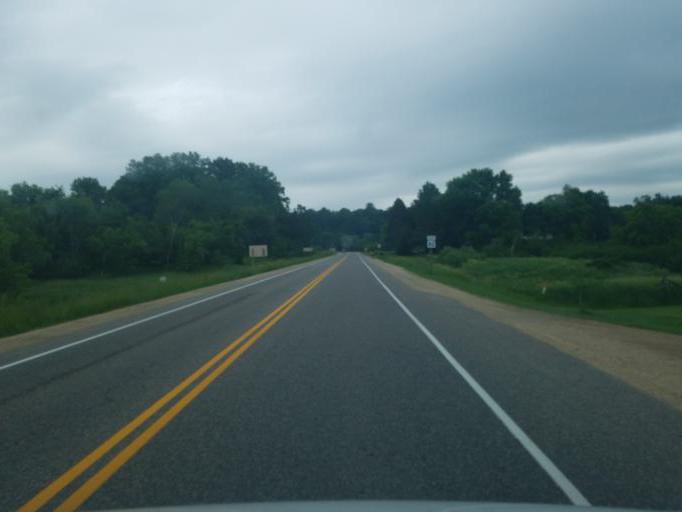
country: US
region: Wisconsin
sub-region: Juneau County
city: Elroy
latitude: 43.7605
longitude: -90.2713
